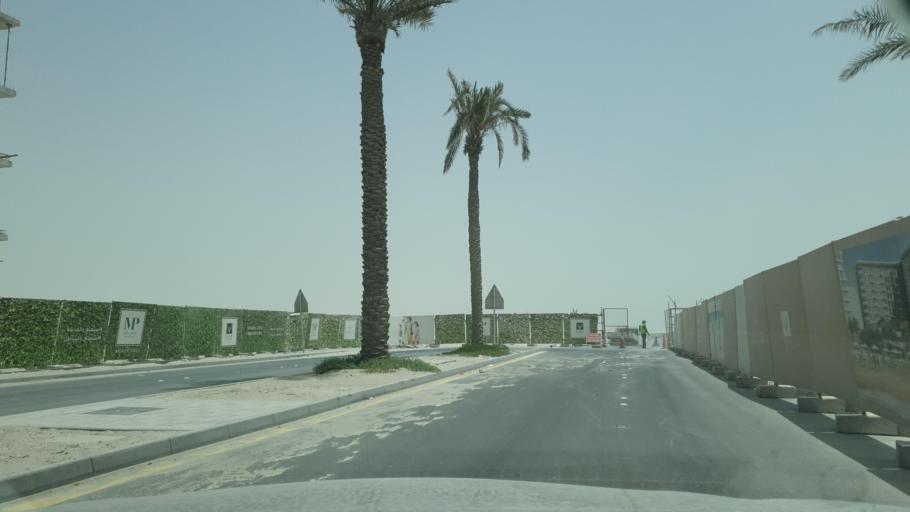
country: BH
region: Muharraq
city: Al Muharraq
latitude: 26.3067
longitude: 50.6461
